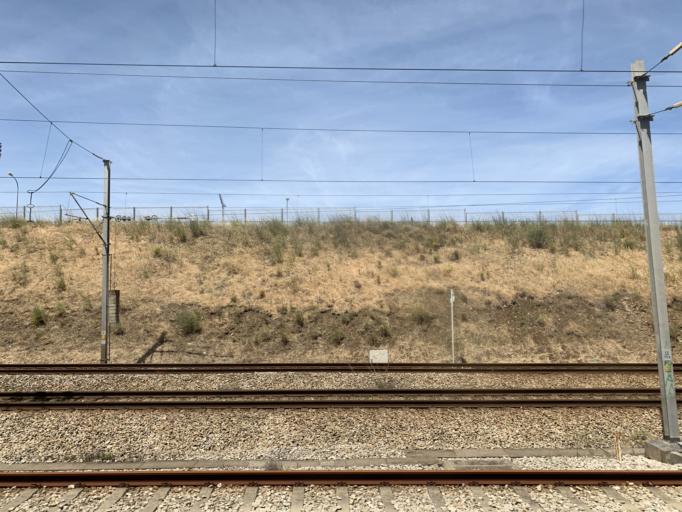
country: PT
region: Lisbon
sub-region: Sintra
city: Queluz
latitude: 38.7527
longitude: -9.2666
